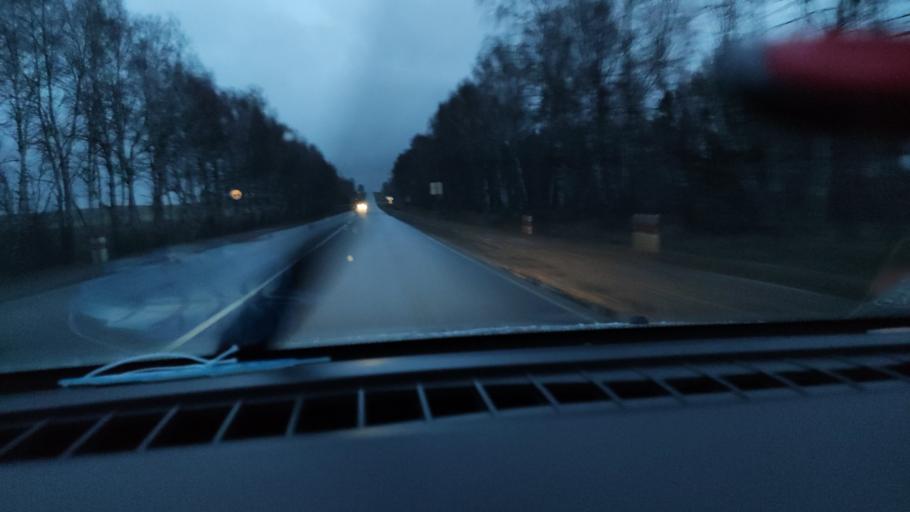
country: RU
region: Udmurtiya
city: Mozhga
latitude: 56.3090
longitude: 52.3357
